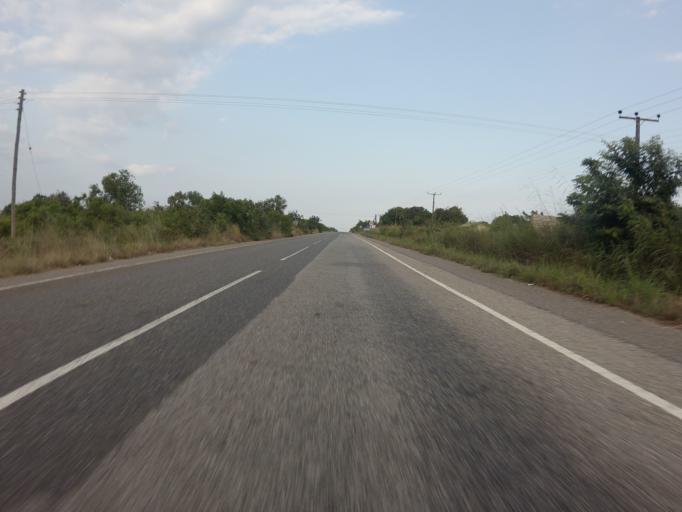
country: GH
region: Volta
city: Anloga
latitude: 6.0859
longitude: 0.5508
